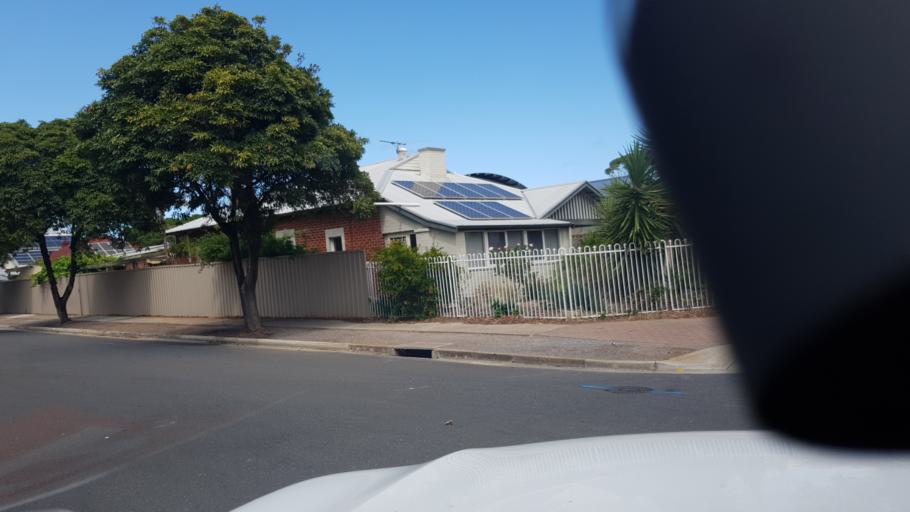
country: AU
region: South Australia
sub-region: Adelaide
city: Brighton
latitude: -35.0120
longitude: 138.5266
